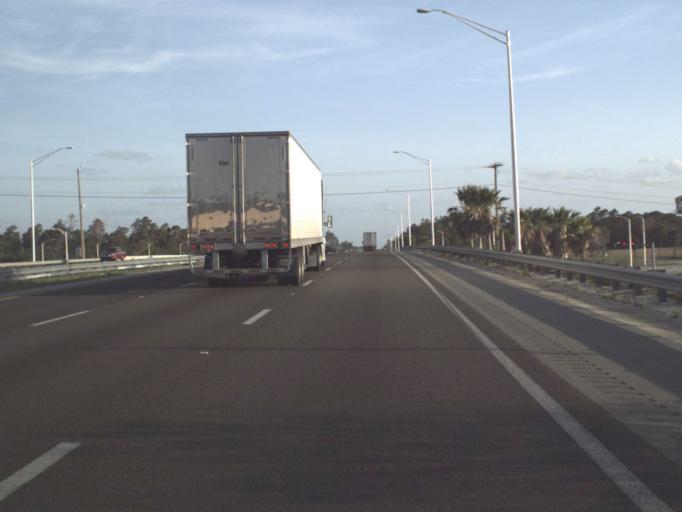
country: US
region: Florida
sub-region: Brevard County
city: Titusville
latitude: 28.6179
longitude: -80.8514
